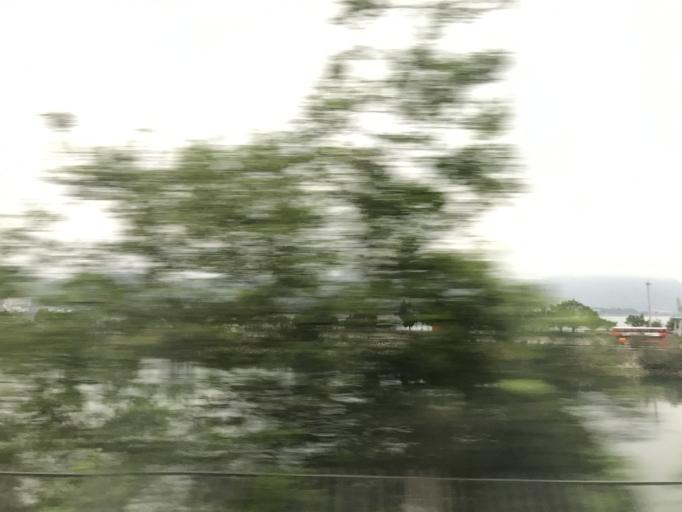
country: HK
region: Tai Po
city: Tai Po
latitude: 22.4369
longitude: 114.1955
